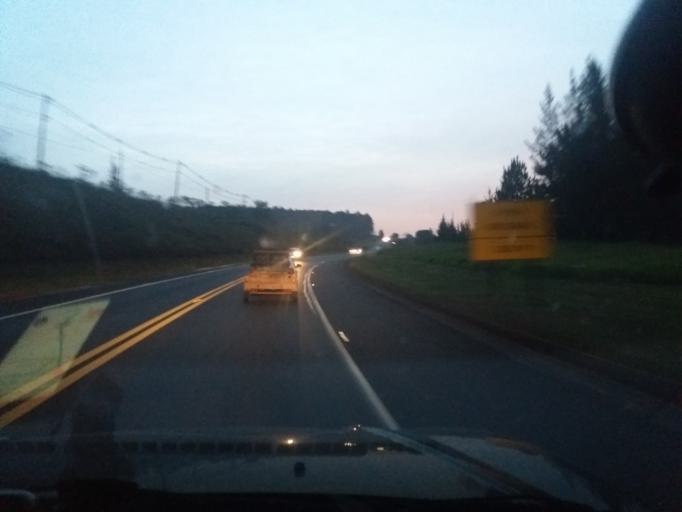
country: BR
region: Sao Paulo
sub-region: Itapeva
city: Itapeva
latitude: -23.9782
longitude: -48.8494
